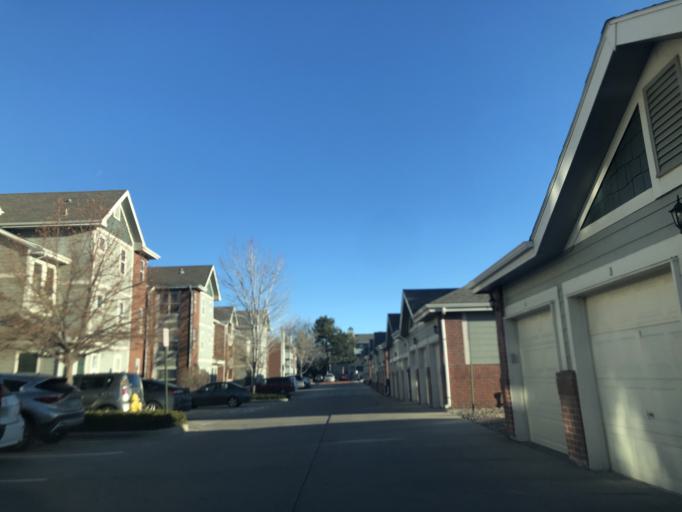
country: US
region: Colorado
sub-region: Adams County
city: Aurora
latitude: 39.7191
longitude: -104.8222
